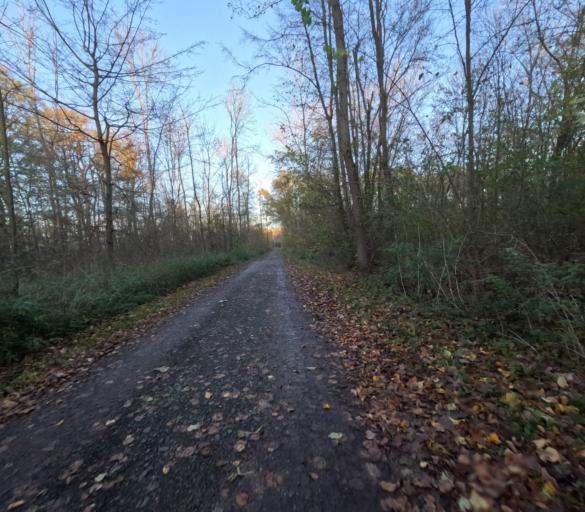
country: DE
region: Saxony
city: Schkeuditz
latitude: 51.3835
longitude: 12.2082
